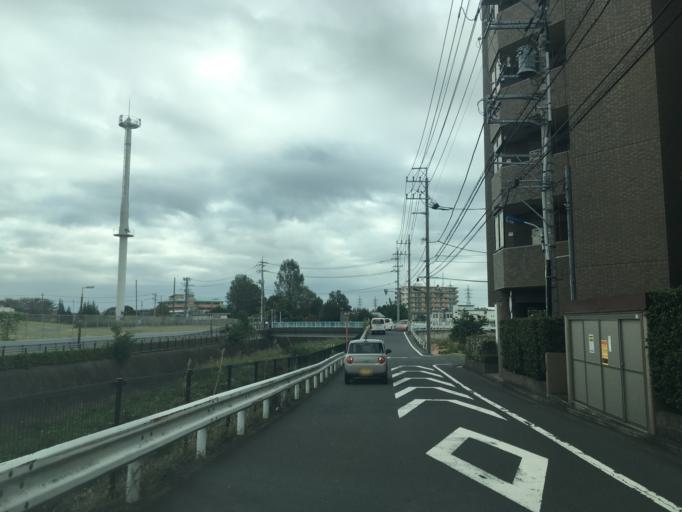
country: JP
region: Tokyo
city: Hino
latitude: 35.7300
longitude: 139.3847
